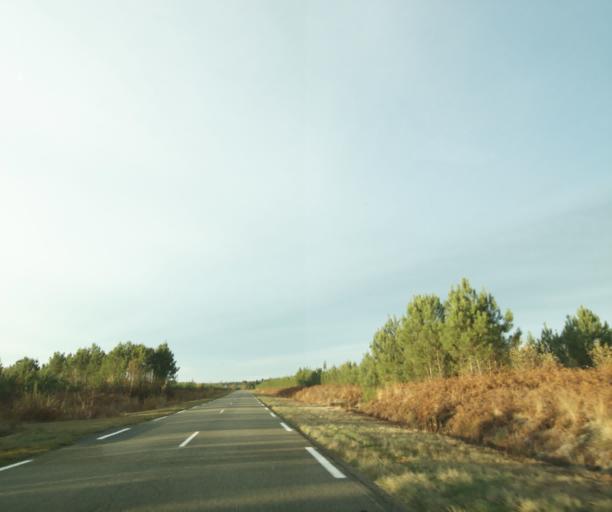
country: FR
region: Aquitaine
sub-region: Departement des Landes
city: Gabarret
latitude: 44.0813
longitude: -0.0717
